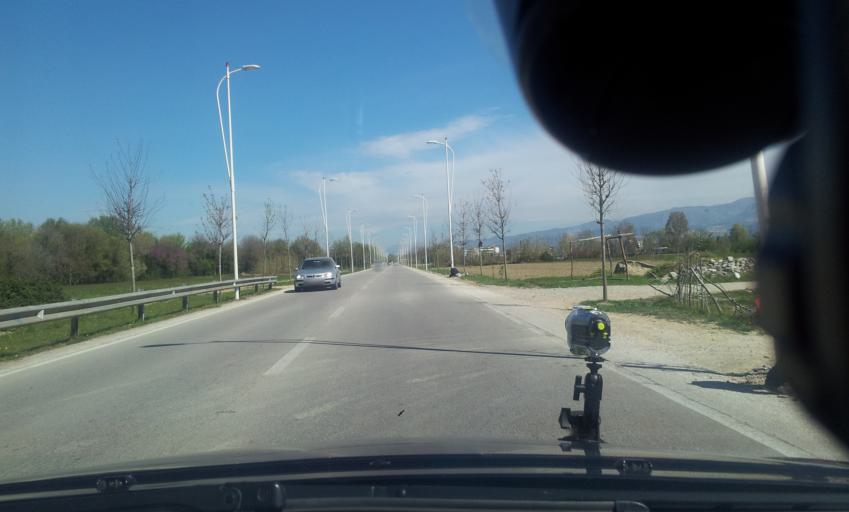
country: AL
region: Tirane
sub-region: Rrethi i Tiranes
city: Berxull
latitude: 41.3929
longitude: 19.7042
